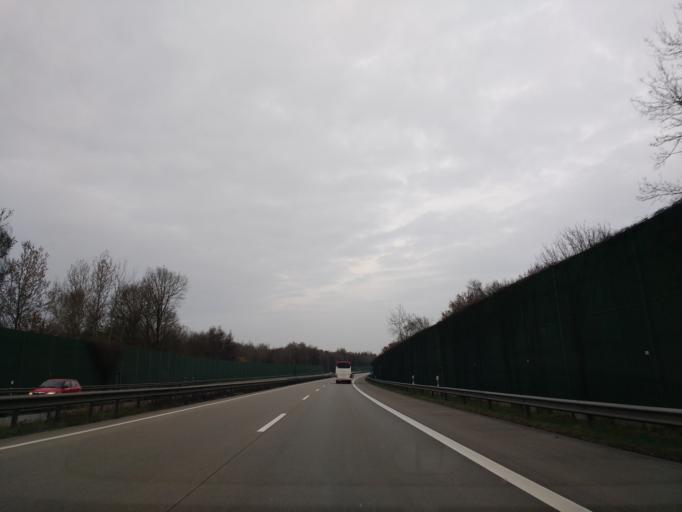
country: DE
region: Lower Saxony
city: Langen
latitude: 53.5752
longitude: 8.6202
